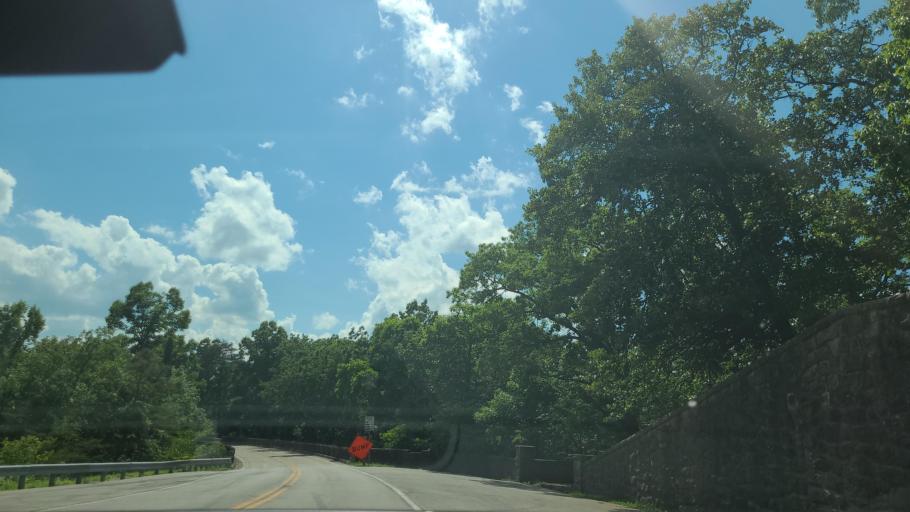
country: US
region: Kentucky
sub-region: Whitley County
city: Williamsburg
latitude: 36.8474
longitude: -84.3089
